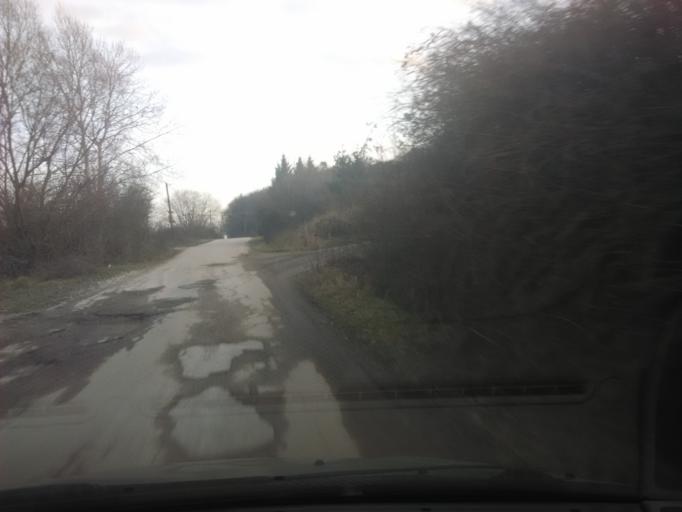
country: SK
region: Nitriansky
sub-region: Okres Nitra
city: Nitra
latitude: 48.3935
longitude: 18.2084
